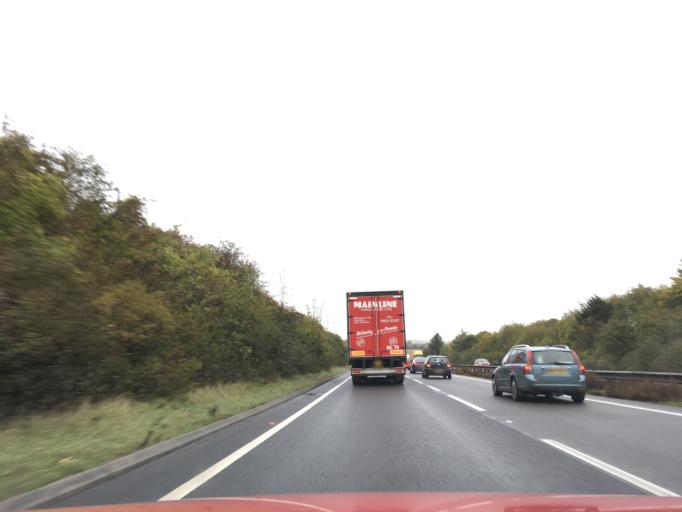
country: GB
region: England
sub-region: Hampshire
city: Kings Worthy
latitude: 51.0970
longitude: -1.3273
